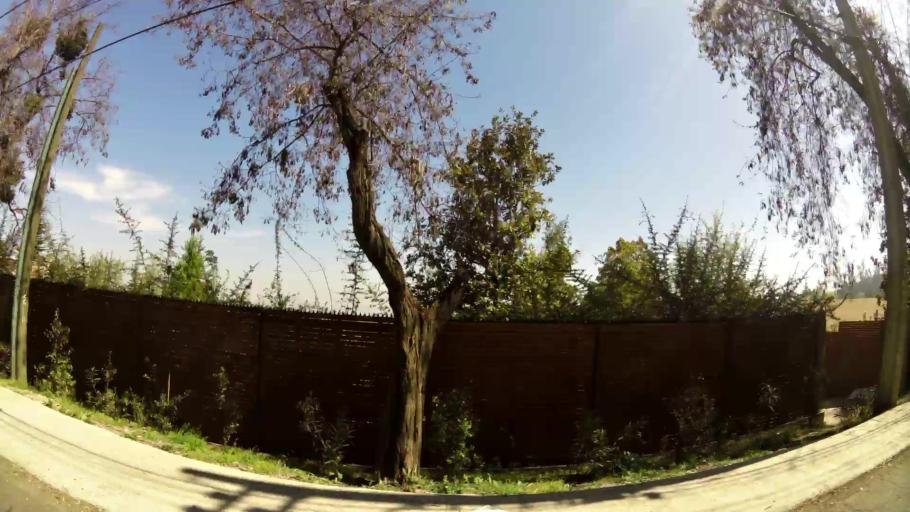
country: CL
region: Santiago Metropolitan
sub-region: Provincia de Santiago
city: Villa Presidente Frei, Nunoa, Santiago, Chile
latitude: -33.4378
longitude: -70.5187
